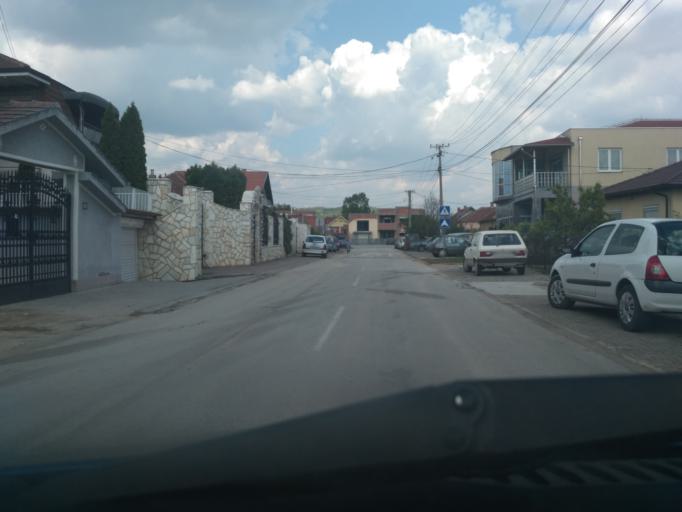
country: RS
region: Central Serbia
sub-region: Pomoravski Okrug
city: Svilajnac
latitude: 44.2353
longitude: 21.2050
